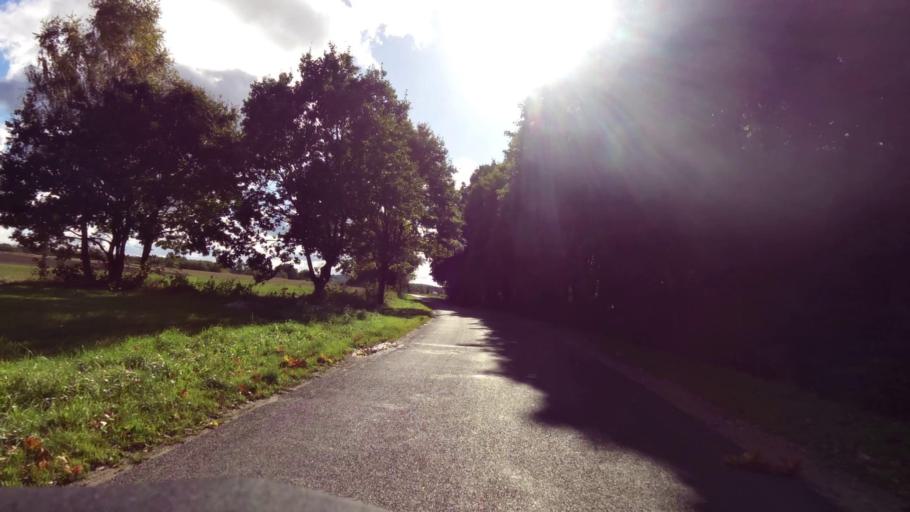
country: PL
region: West Pomeranian Voivodeship
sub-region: Powiat bialogardzki
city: Bialogard
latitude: 53.9963
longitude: 16.0627
